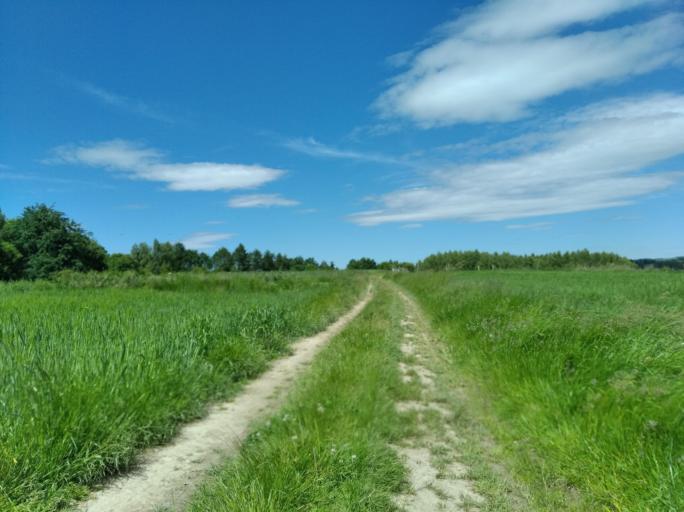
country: PL
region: Subcarpathian Voivodeship
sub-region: Powiat strzyzowski
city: Strzyzow
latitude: 49.8418
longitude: 21.7984
